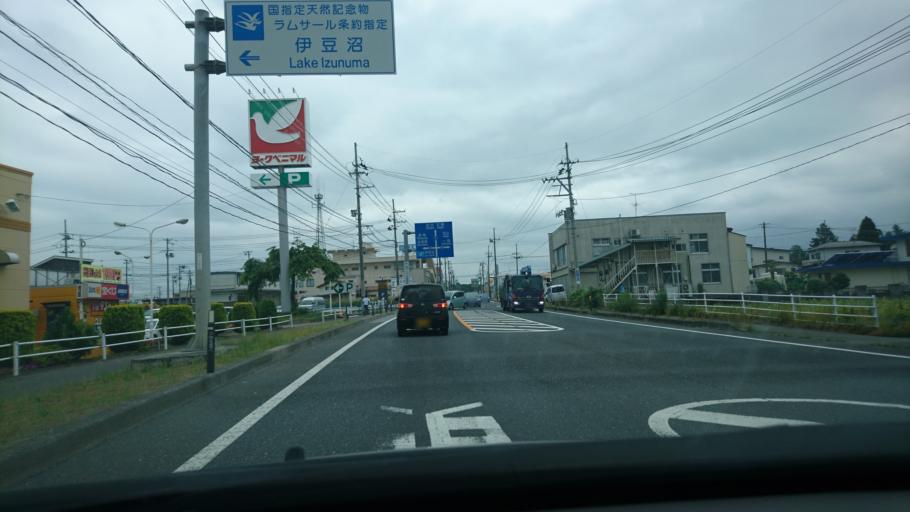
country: JP
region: Miyagi
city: Furukawa
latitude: 38.7364
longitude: 141.0224
